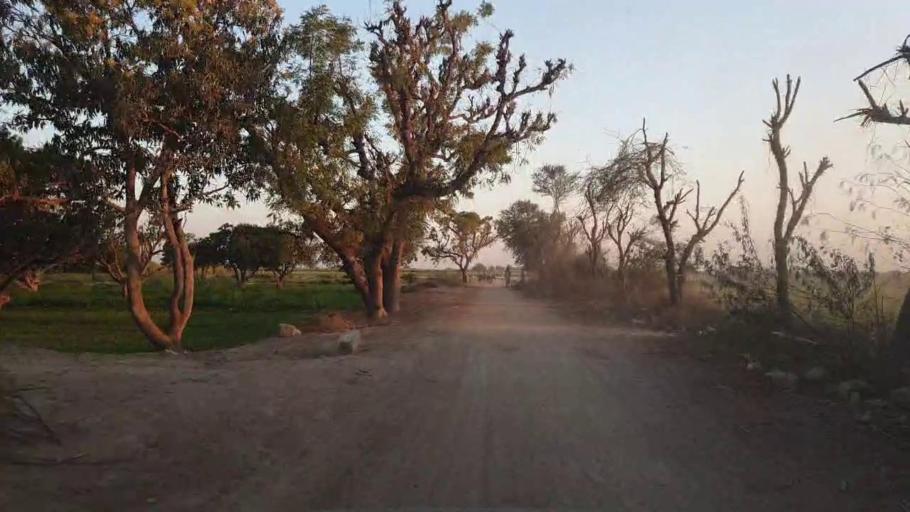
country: PK
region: Sindh
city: Tando Allahyar
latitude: 25.3631
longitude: 68.7287
